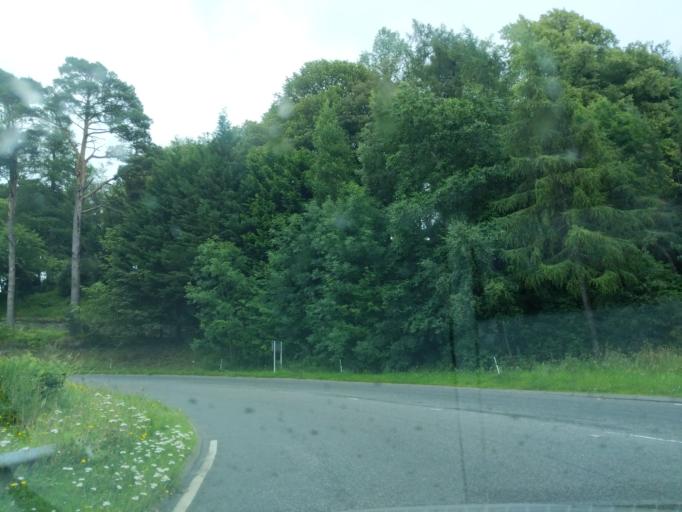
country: GB
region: Scotland
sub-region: Moray
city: Rothes
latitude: 57.4875
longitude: -3.1931
